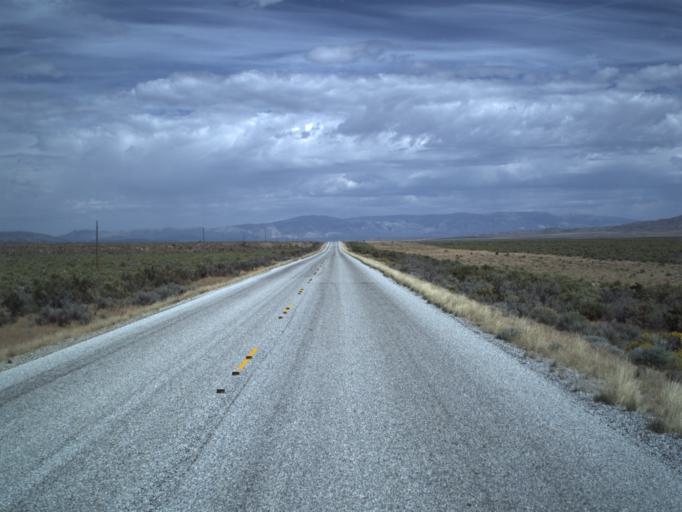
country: US
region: Utah
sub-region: Tooele County
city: Wendover
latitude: 41.5539
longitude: -113.5856
